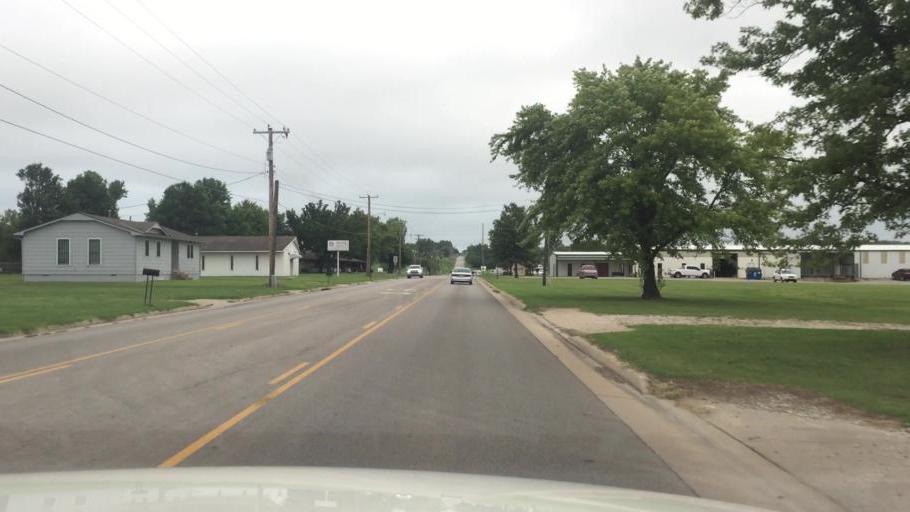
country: US
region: Kansas
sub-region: Montgomery County
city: Coffeyville
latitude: 37.0474
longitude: -95.6473
